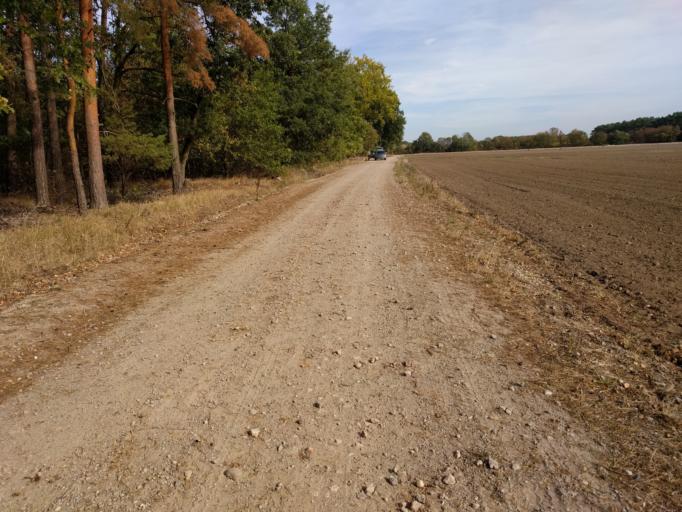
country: DE
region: Brandenburg
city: Ziesar
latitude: 52.2097
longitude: 12.2689
